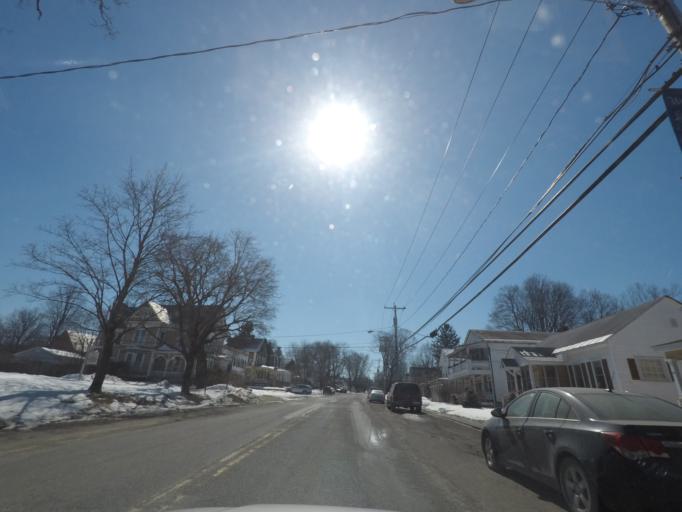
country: US
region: New York
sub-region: Saratoga County
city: Stillwater
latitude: 42.9016
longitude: -73.5627
